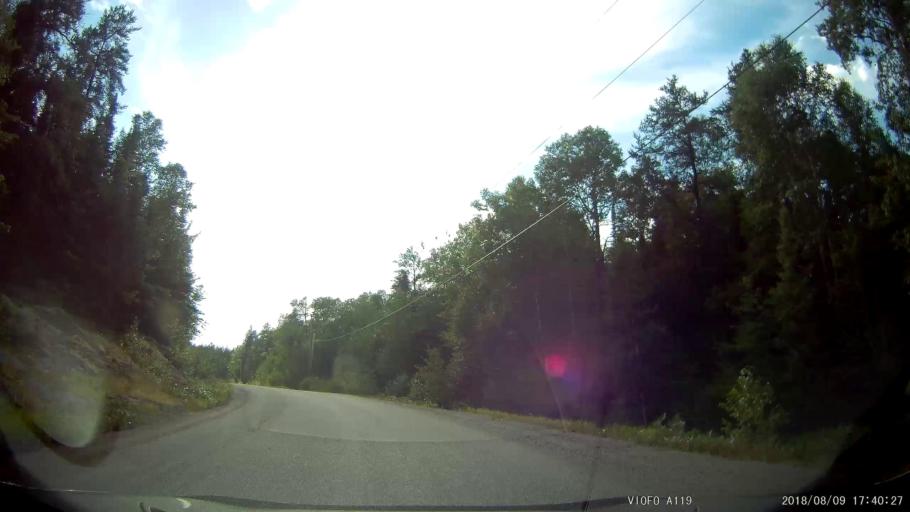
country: CA
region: Ontario
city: Rayside-Balfour
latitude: 46.6076
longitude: -81.5021
